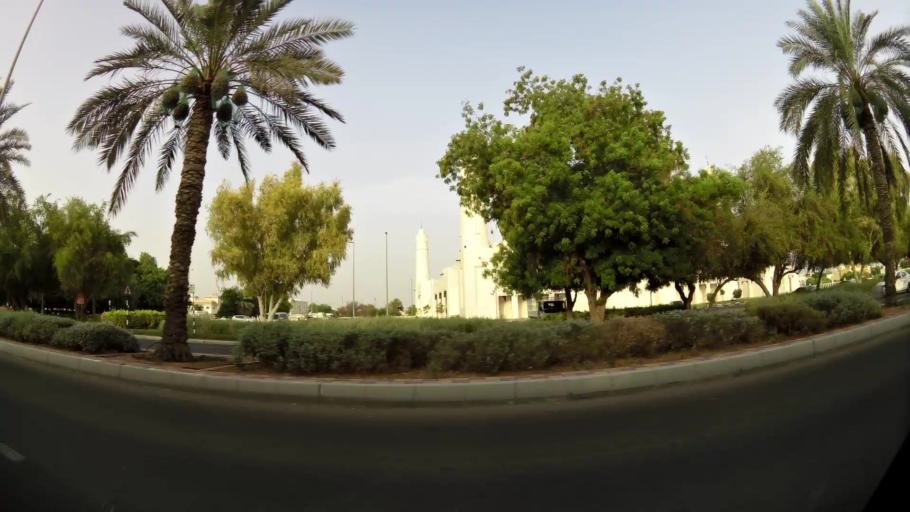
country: OM
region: Al Buraimi
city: Al Buraymi
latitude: 24.2450
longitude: 55.7392
